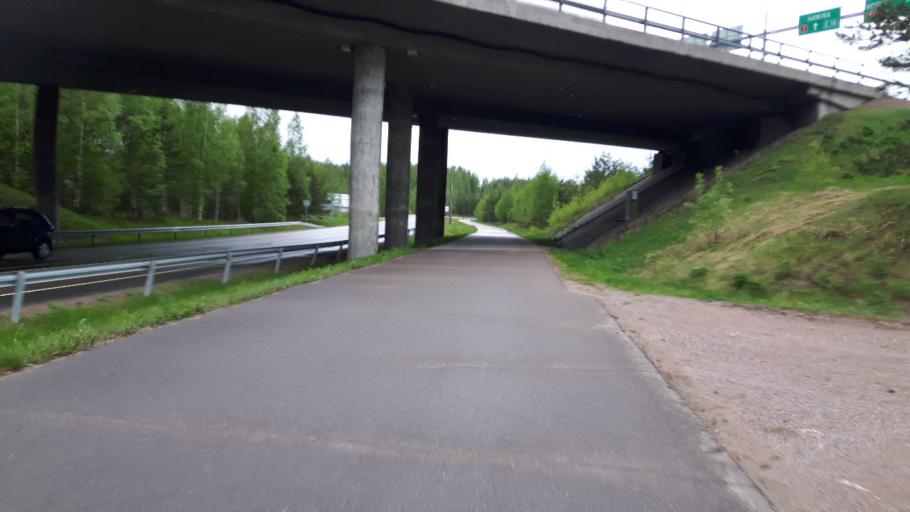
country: FI
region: Kymenlaakso
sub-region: Kotka-Hamina
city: Karhula
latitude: 60.5594
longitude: 27.0071
